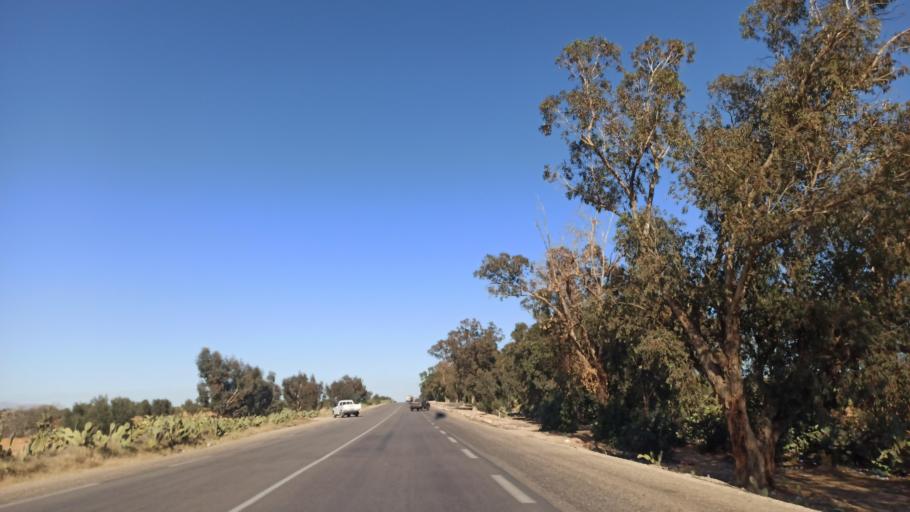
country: TN
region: Sidi Bu Zayd
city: Jilma
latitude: 35.1627
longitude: 9.3678
